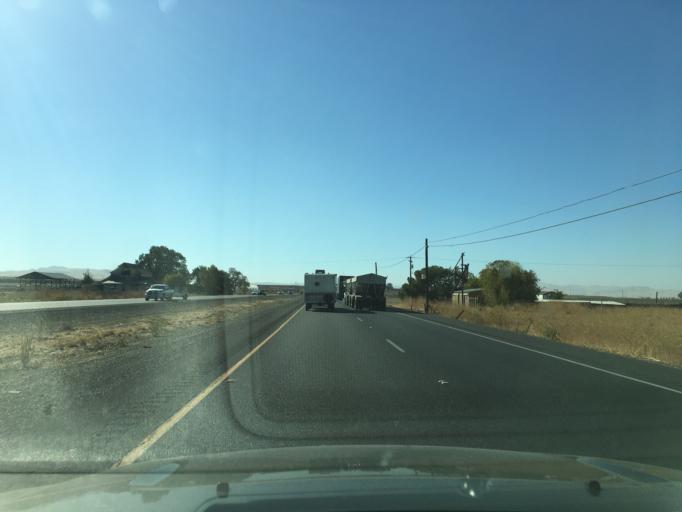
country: US
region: California
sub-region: Merced County
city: Los Banos
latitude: 37.0566
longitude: -120.9333
